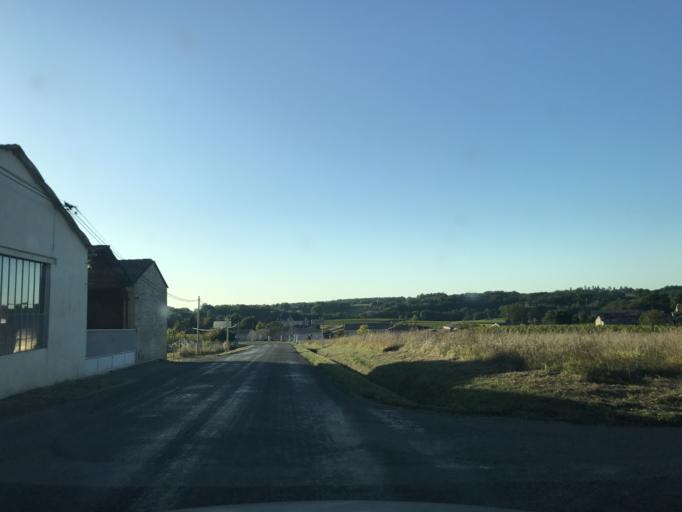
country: FR
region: Aquitaine
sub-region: Departement de la Gironde
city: Lussac
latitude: 44.8987
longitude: -0.0665
